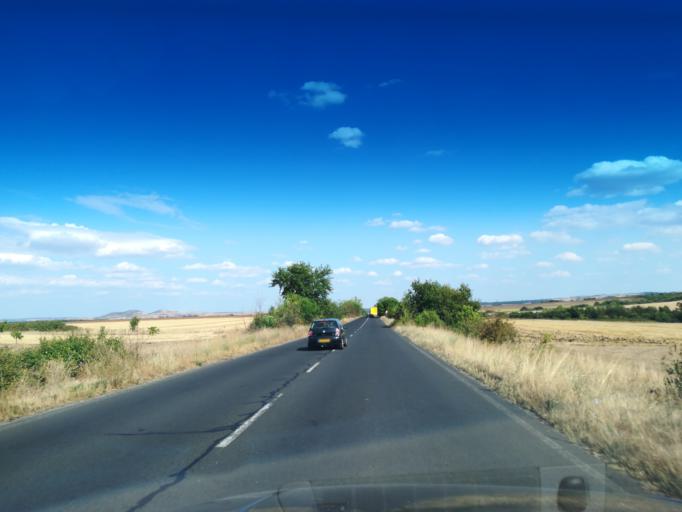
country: BG
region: Stara Zagora
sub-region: Obshtina Chirpan
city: Chirpan
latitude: 42.0571
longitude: 25.2927
